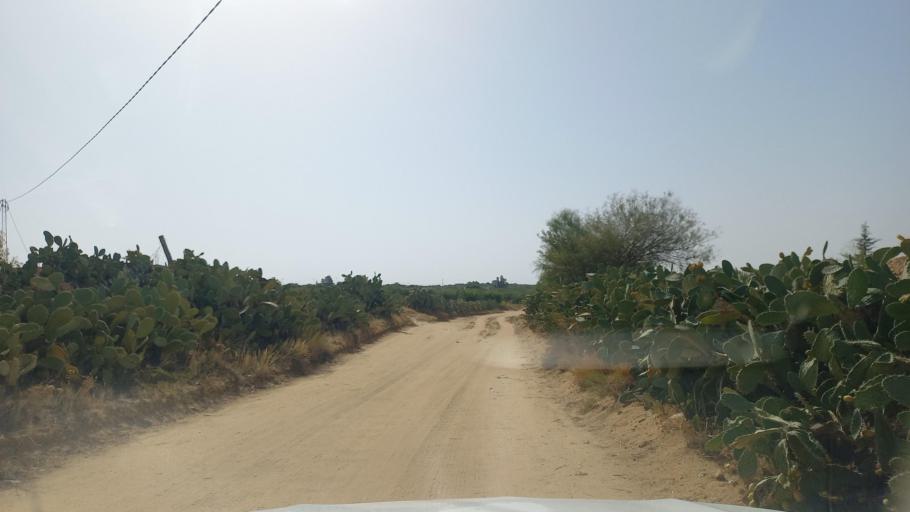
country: TN
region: Al Qasrayn
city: Kasserine
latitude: 35.2444
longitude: 9.0332
